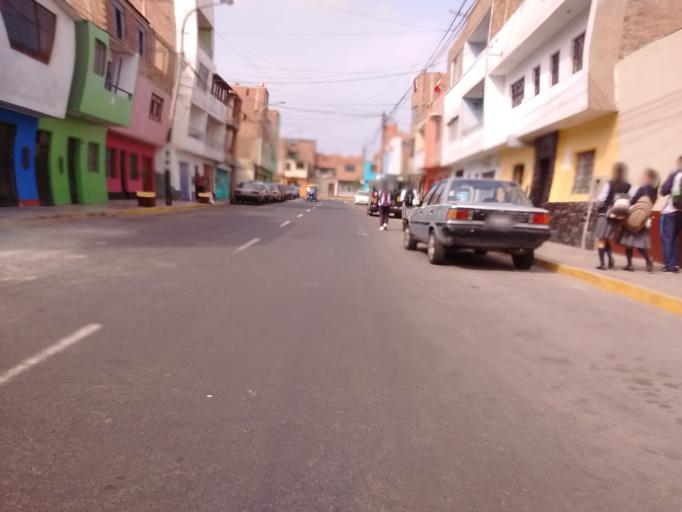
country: PE
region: Callao
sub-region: Callao
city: Callao
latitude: -12.0412
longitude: -77.0949
